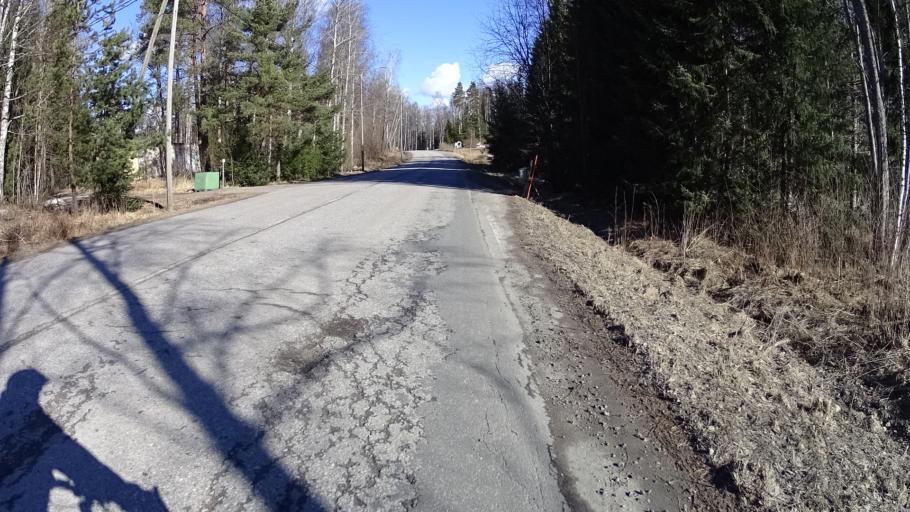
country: FI
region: Uusimaa
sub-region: Helsinki
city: Kauniainen
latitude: 60.2699
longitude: 24.7098
